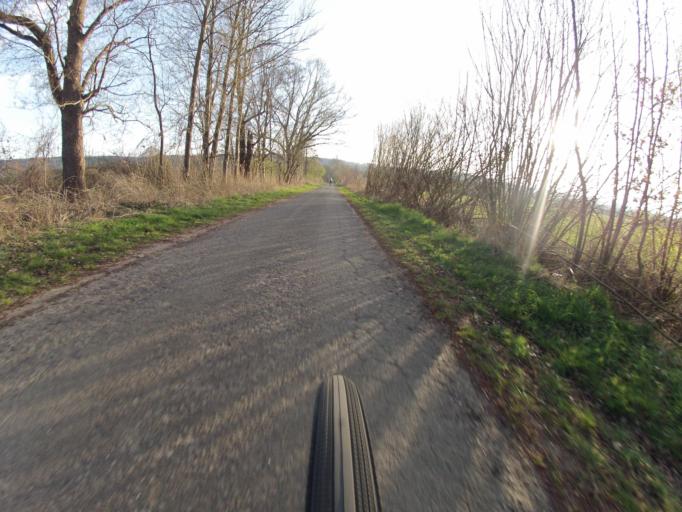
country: DE
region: North Rhine-Westphalia
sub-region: Regierungsbezirk Munster
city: Tecklenburg
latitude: 52.2439
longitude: 7.7687
